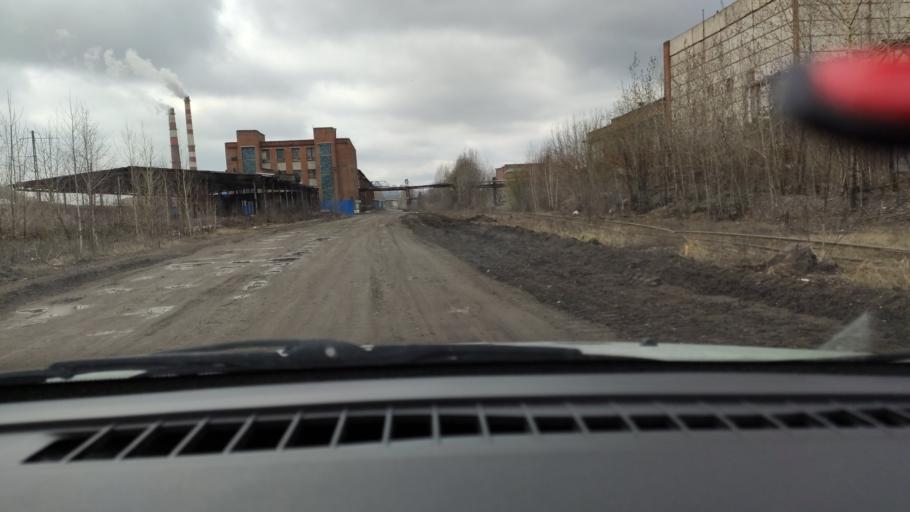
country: RU
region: Perm
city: Perm
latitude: 58.0509
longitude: 56.3198
